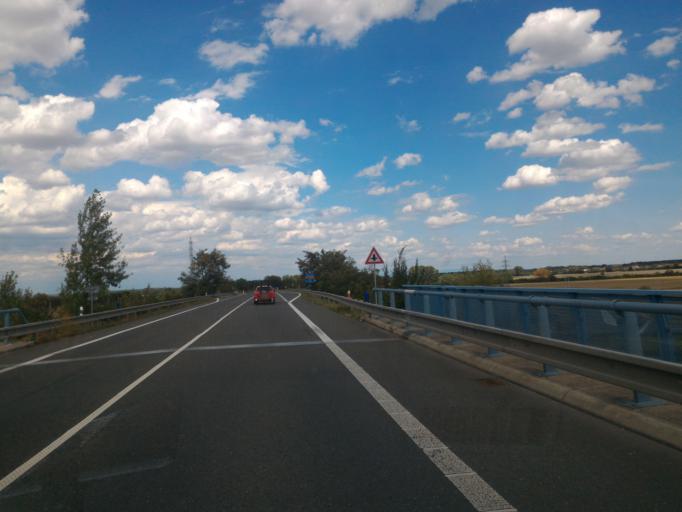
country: CZ
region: Central Bohemia
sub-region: Okres Nymburk
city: Podebrady
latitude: 50.1678
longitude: 15.0911
